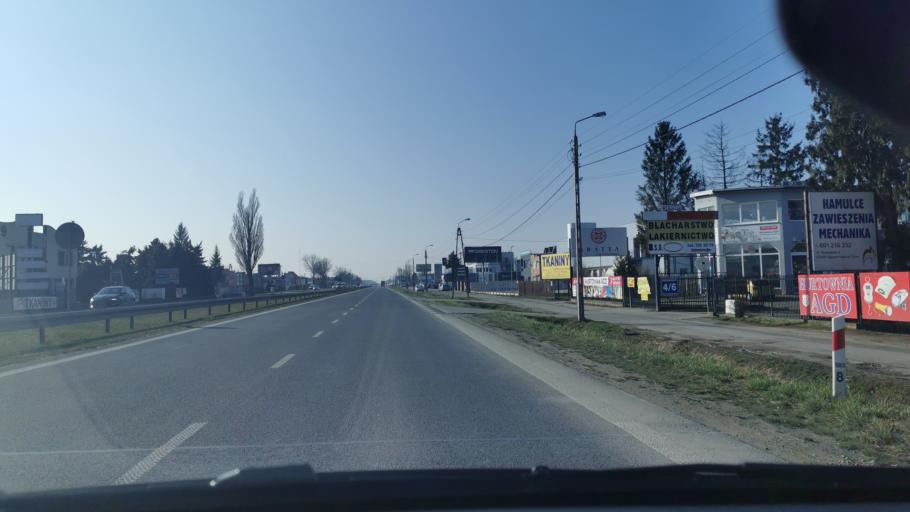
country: PL
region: Masovian Voivodeship
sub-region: Powiat pruszkowski
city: Nowe Grocholice
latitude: 52.1234
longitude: 20.8944
